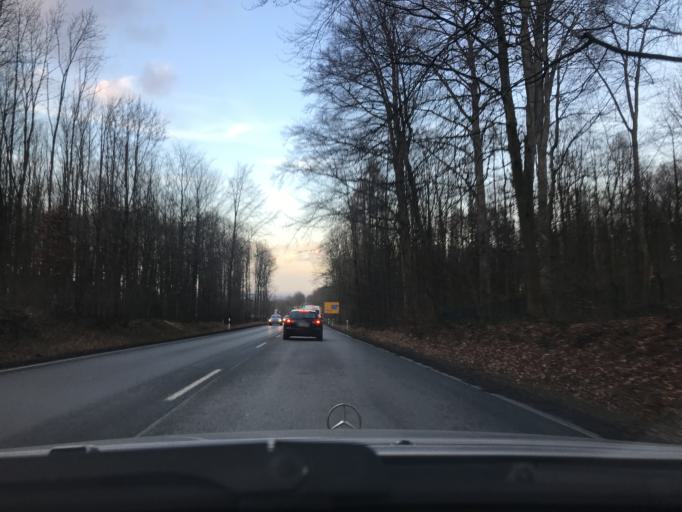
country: DE
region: North Rhine-Westphalia
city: Wickede
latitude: 51.5168
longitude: 7.8874
